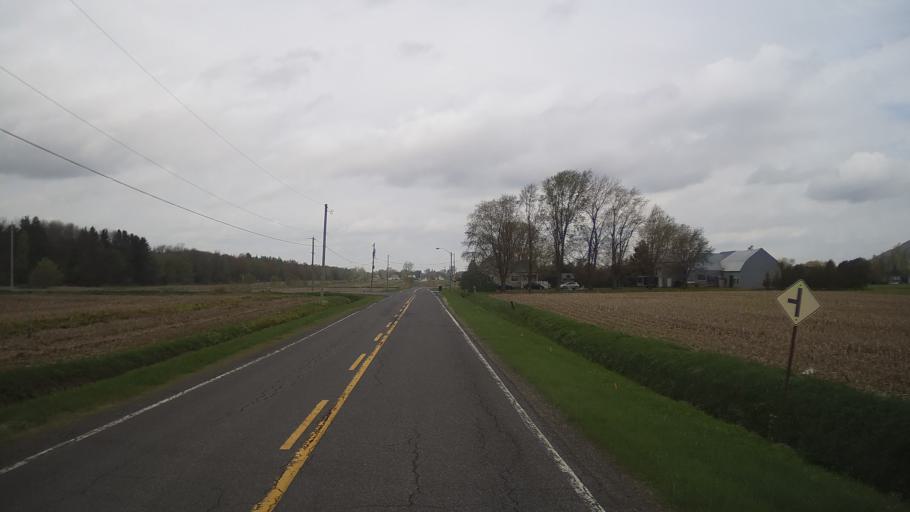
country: CA
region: Quebec
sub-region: Monteregie
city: Marieville
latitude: 45.3239
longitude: -73.1413
